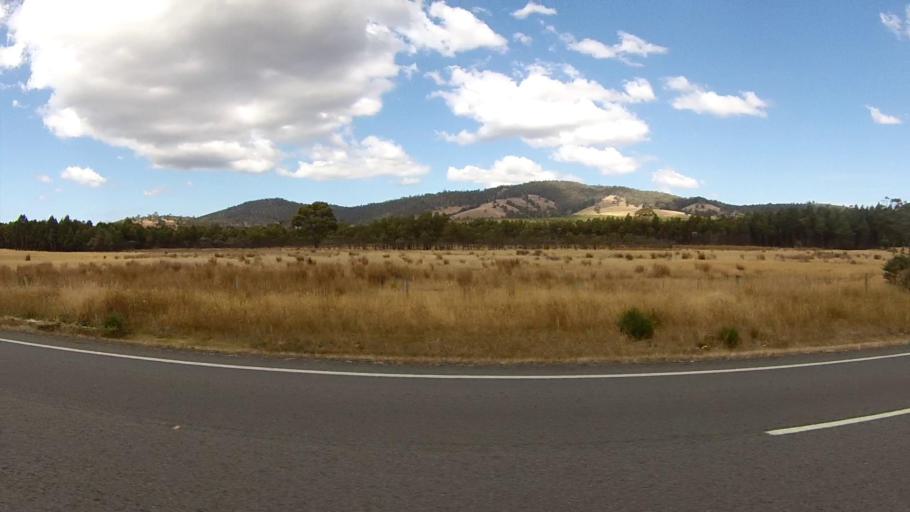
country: AU
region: Tasmania
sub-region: Sorell
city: Sorell
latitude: -42.6405
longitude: 147.5805
